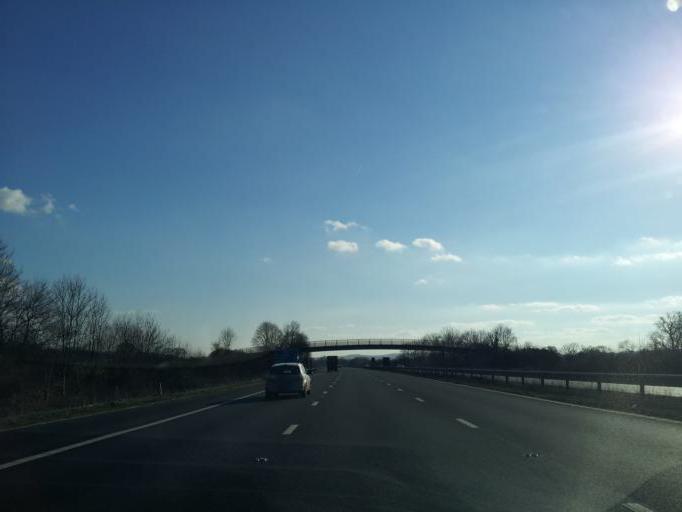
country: GB
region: England
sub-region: Devon
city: Uffculme
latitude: 50.9111
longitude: -3.3634
